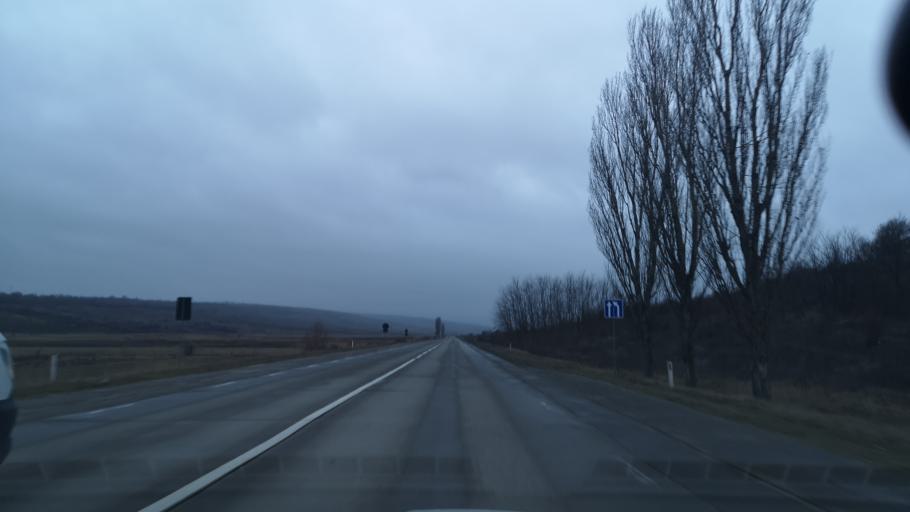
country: MD
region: Taraclia
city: Mindresti
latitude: 47.3994
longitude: 28.3001
